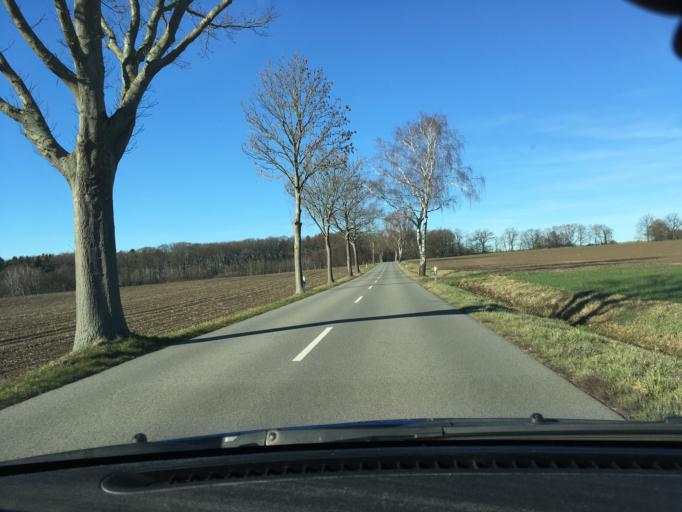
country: DE
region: Lower Saxony
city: Schwienau
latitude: 52.9706
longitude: 10.4549
